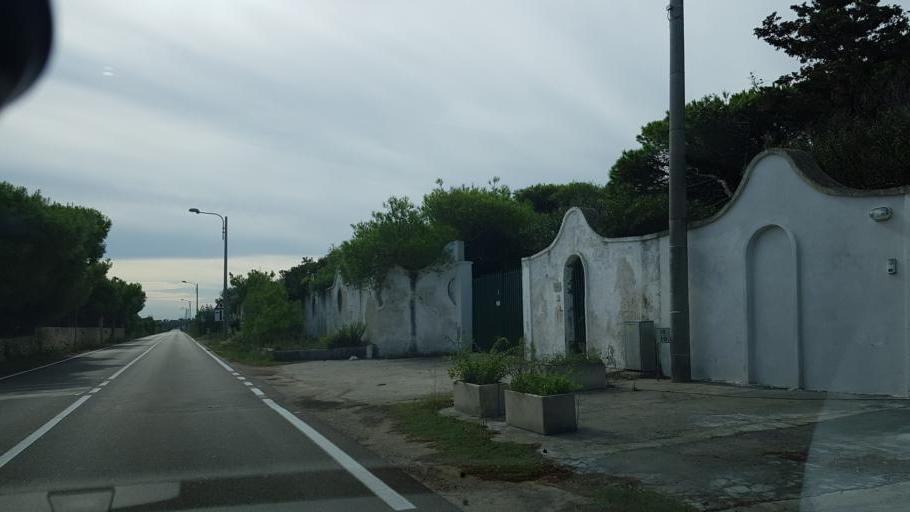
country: IT
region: Apulia
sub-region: Provincia di Lecce
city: Melendugno
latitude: 40.3206
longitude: 18.3795
